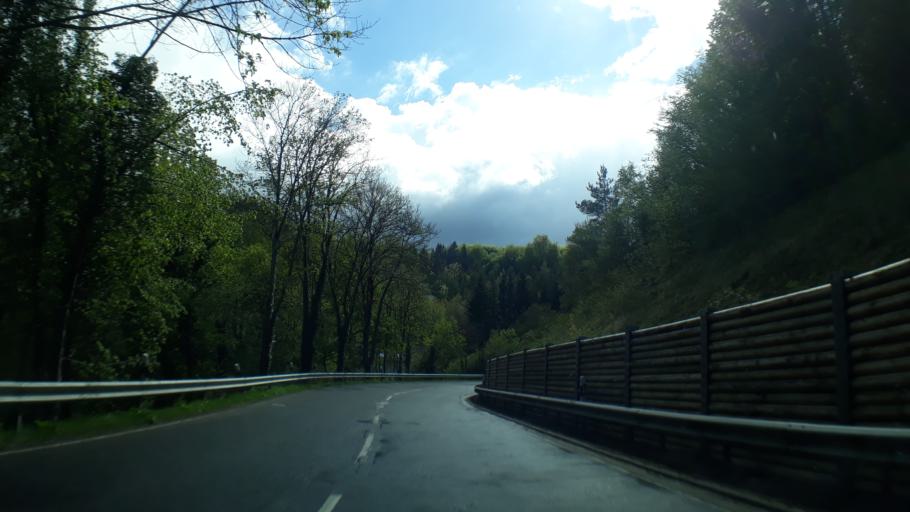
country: DE
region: North Rhine-Westphalia
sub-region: Regierungsbezirk Koln
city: Kall
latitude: 50.5193
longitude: 6.5625
